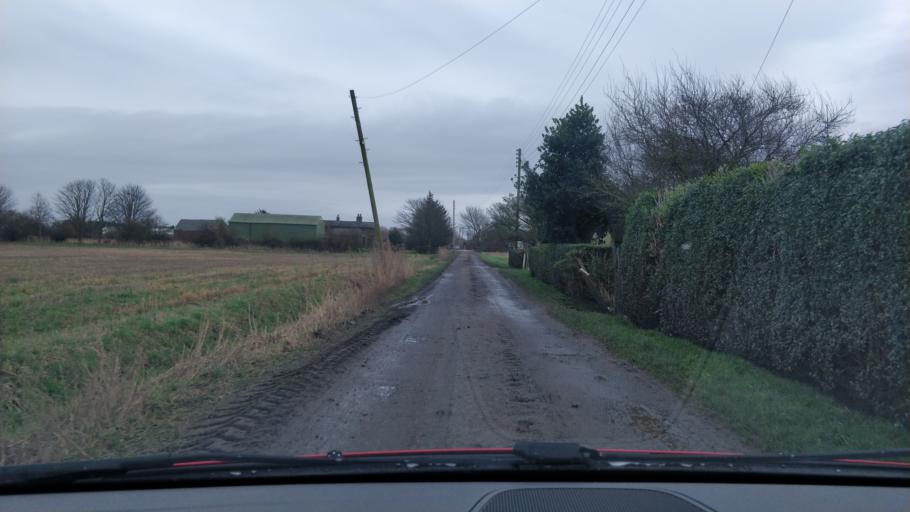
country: GB
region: England
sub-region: Lancashire
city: Banks
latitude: 53.6848
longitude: -2.9291
